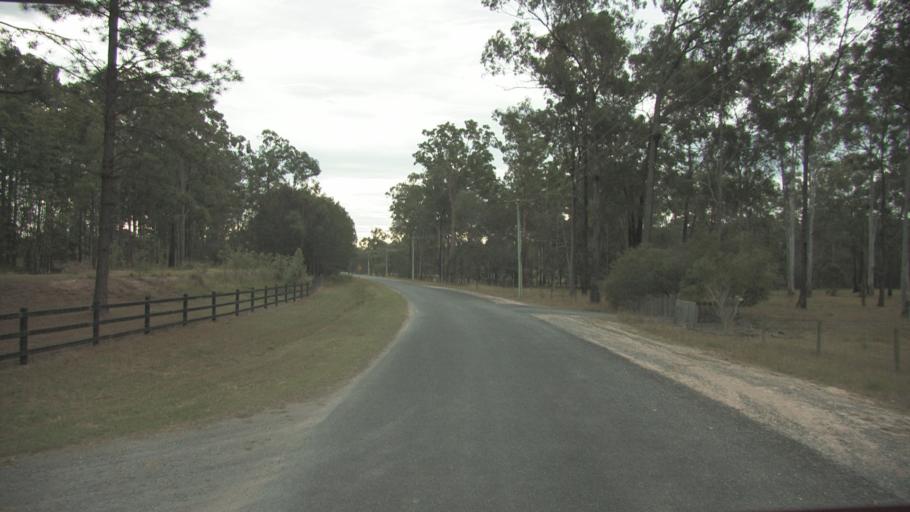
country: AU
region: Queensland
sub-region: Logan
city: Chambers Flat
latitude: -27.7939
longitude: 153.1252
